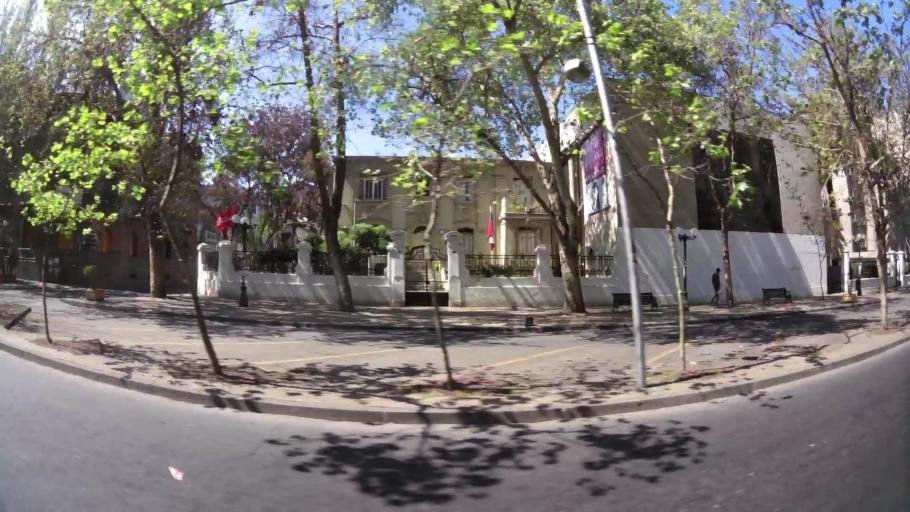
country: CL
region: Santiago Metropolitan
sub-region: Provincia de Santiago
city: Santiago
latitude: -33.4392
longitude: -70.6346
